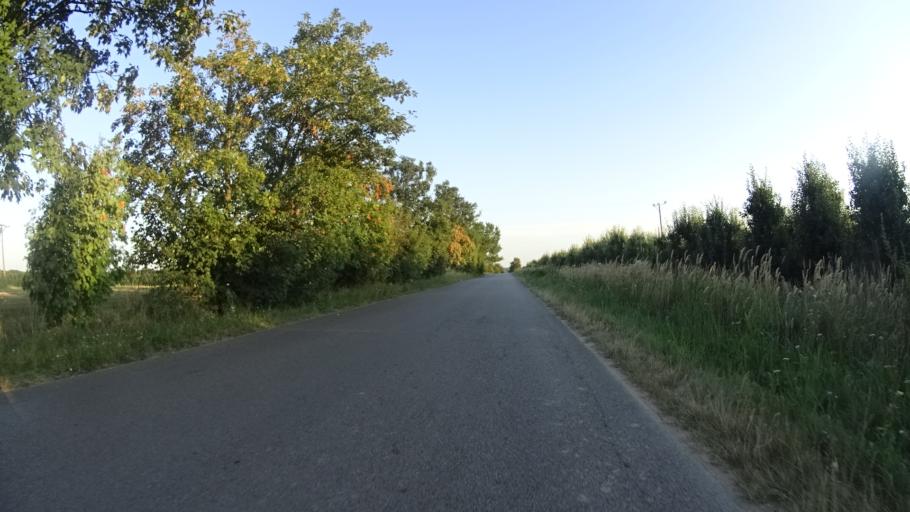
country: PL
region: Masovian Voivodeship
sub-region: Powiat bialobrzeski
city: Wysmierzyce
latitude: 51.6655
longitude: 20.8312
